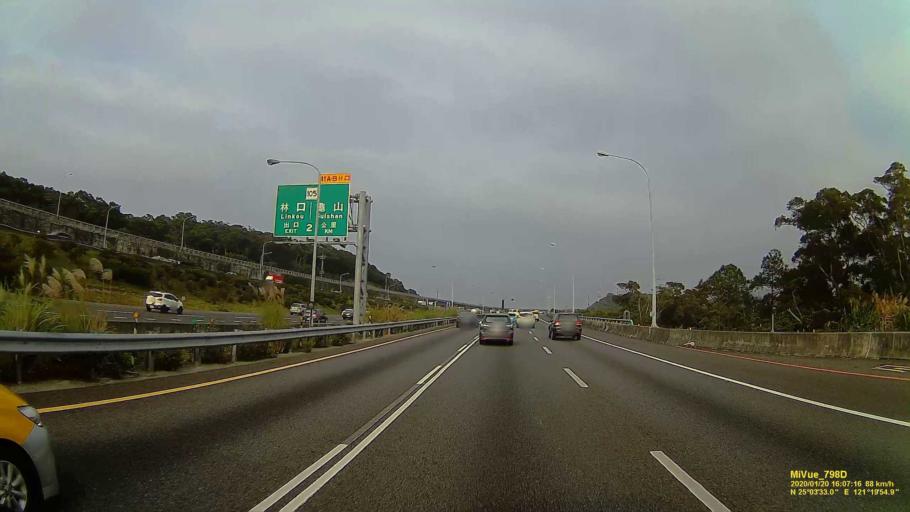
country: TW
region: Taiwan
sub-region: Taoyuan
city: Taoyuan
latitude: 25.0596
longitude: 121.3325
